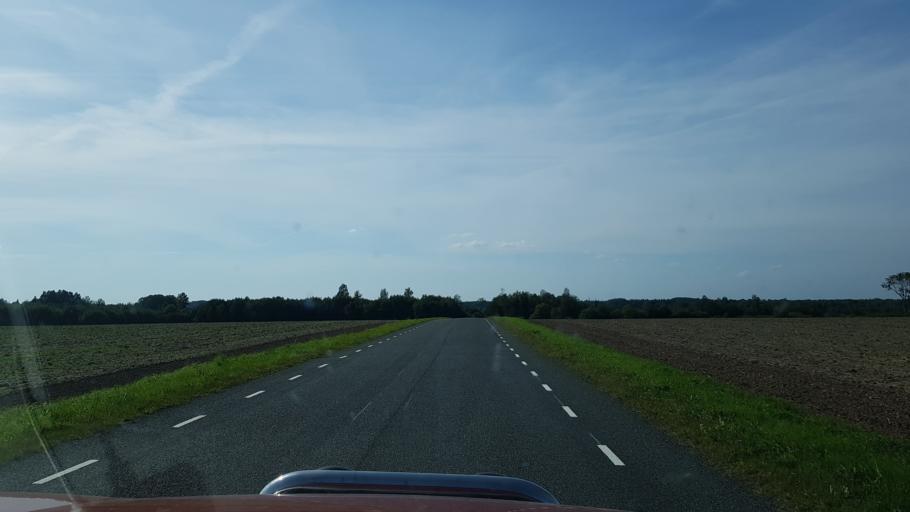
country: EE
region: Viljandimaa
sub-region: Abja vald
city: Abja-Paluoja
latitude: 58.3378
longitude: 25.2572
